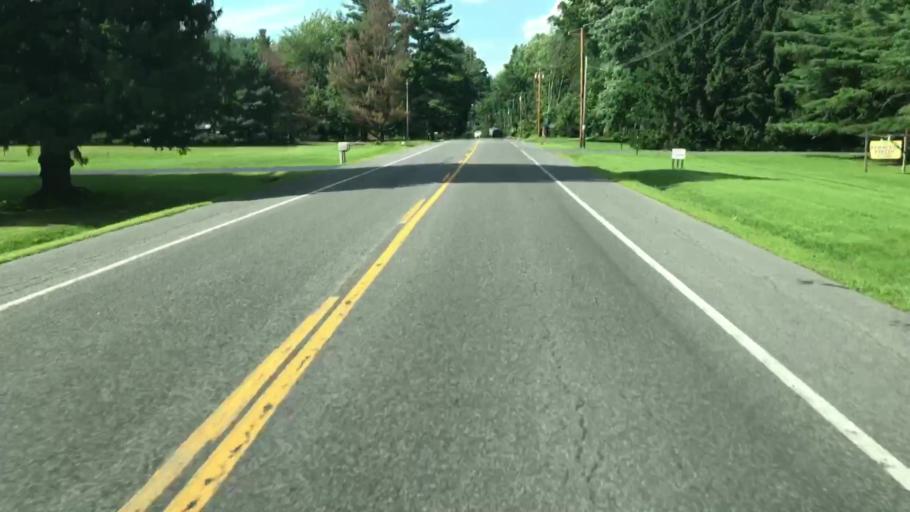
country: US
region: New York
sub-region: Onondaga County
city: Liverpool
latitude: 43.1605
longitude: -76.1946
